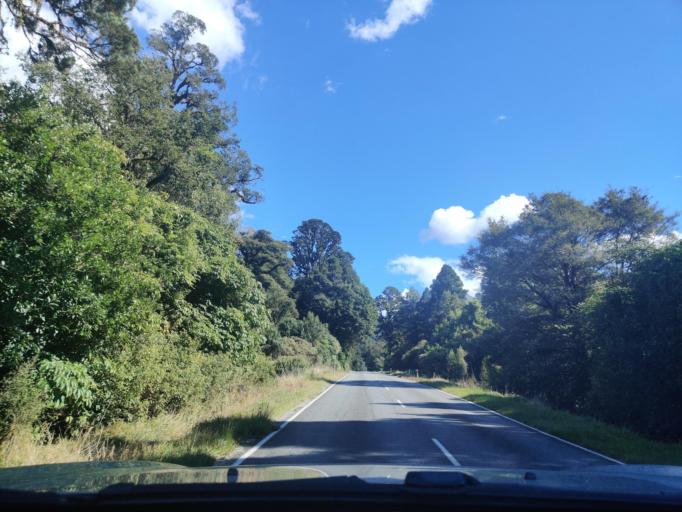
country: NZ
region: Otago
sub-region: Queenstown-Lakes District
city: Wanaka
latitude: -43.9707
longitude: 169.3826
